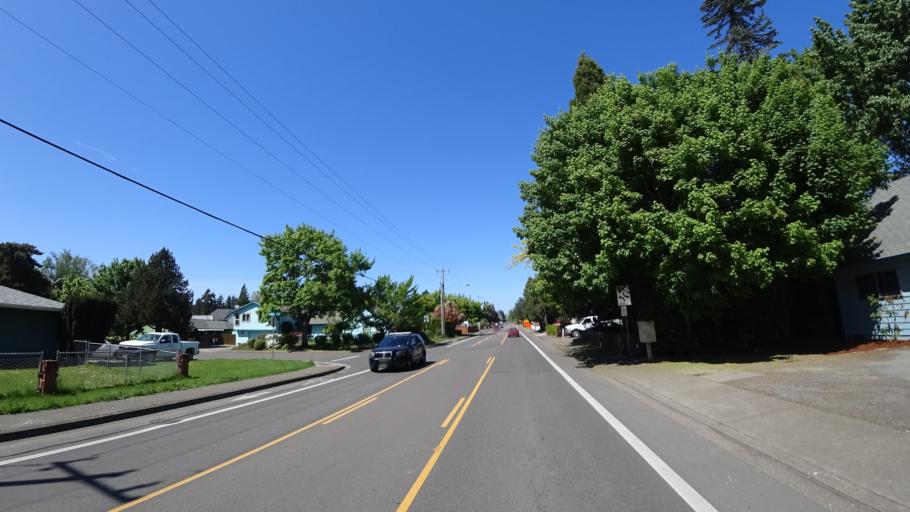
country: US
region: Oregon
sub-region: Washington County
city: Hillsboro
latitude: 45.5143
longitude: -122.9497
